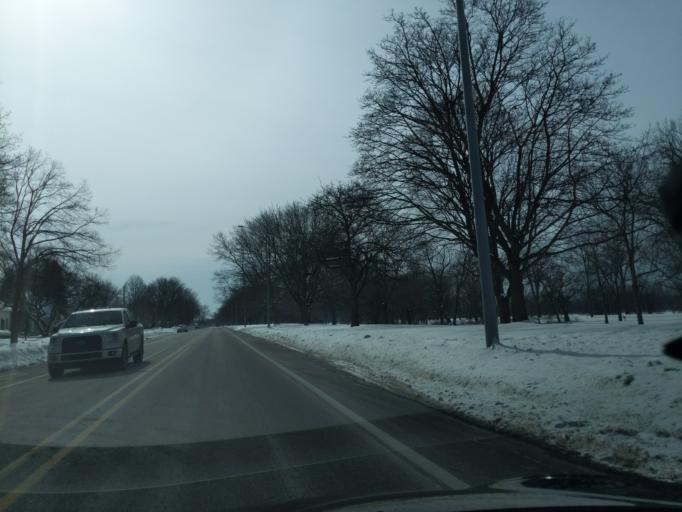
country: US
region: Michigan
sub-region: Kent County
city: Comstock Park
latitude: 43.0053
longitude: -85.6687
